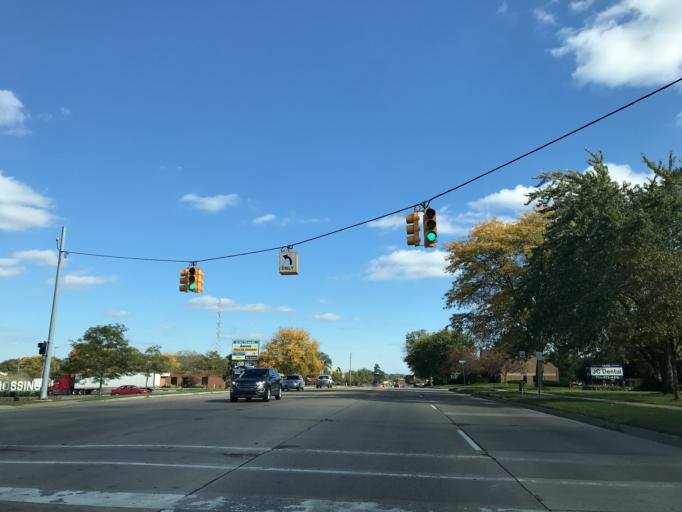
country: US
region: Michigan
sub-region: Washtenaw County
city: Ypsilanti
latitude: 42.2516
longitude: -83.6688
